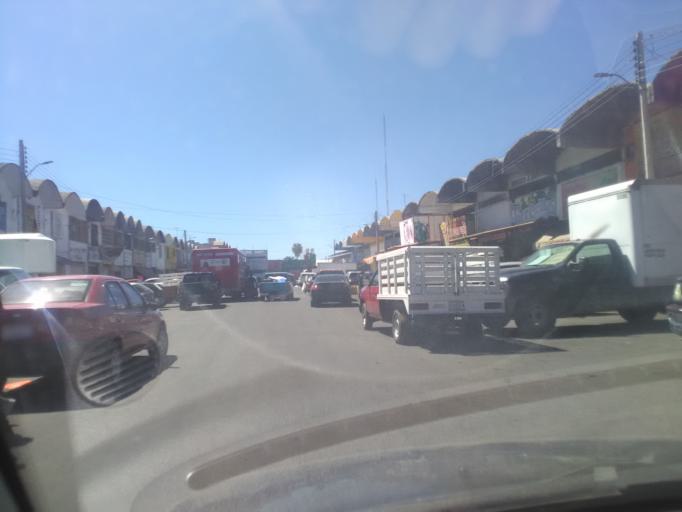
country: MX
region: Durango
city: Victoria de Durango
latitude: 24.0155
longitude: -104.6605
